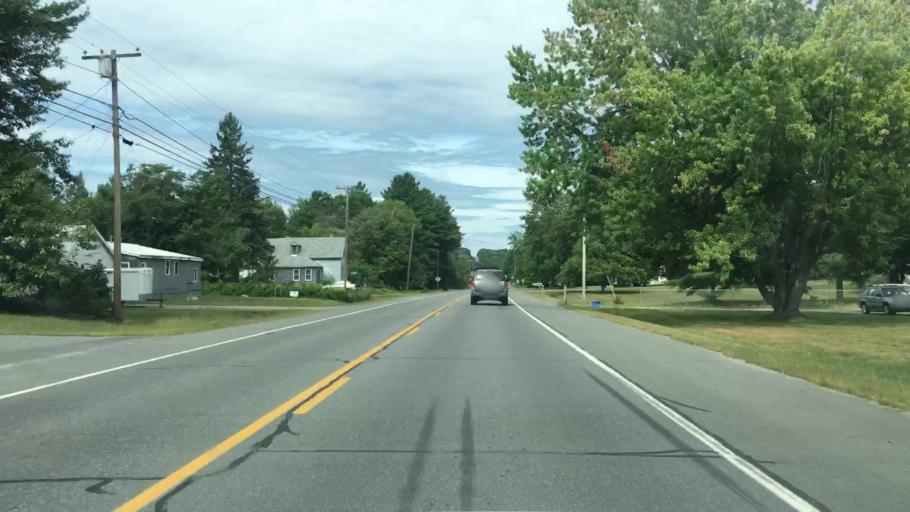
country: US
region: Maine
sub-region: Piscataquis County
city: Milo
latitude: 45.2667
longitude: -68.9945
